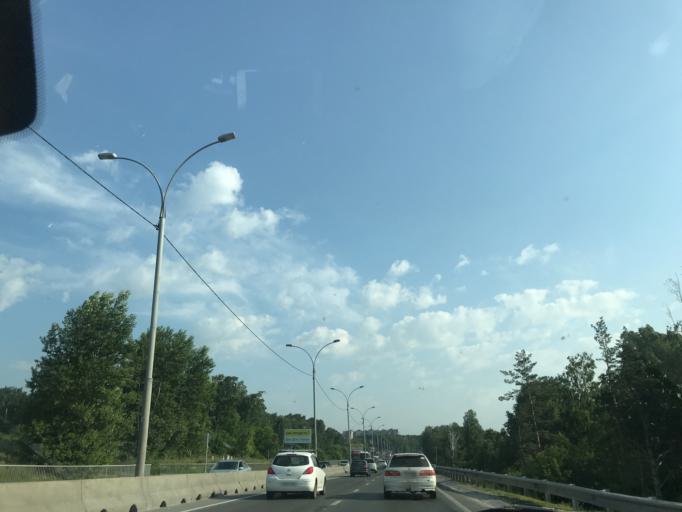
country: RU
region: Novosibirsk
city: Akademgorodok
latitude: 54.8143
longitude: 83.0891
